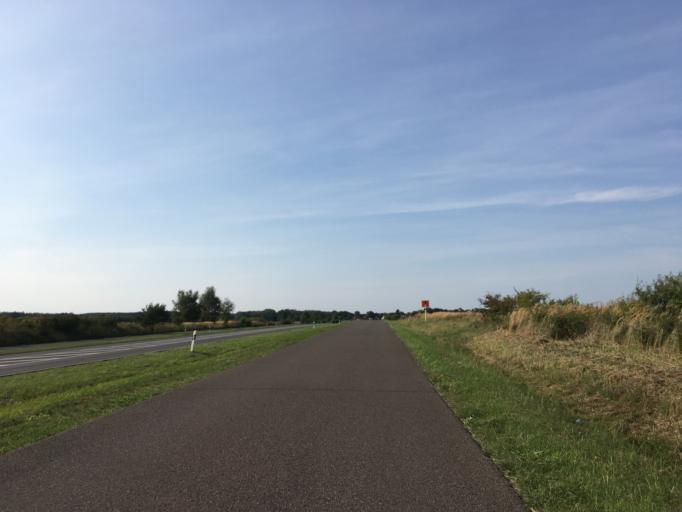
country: DE
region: Brandenburg
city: Brieskow-Finkenheerd
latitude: 52.2759
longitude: 14.5616
